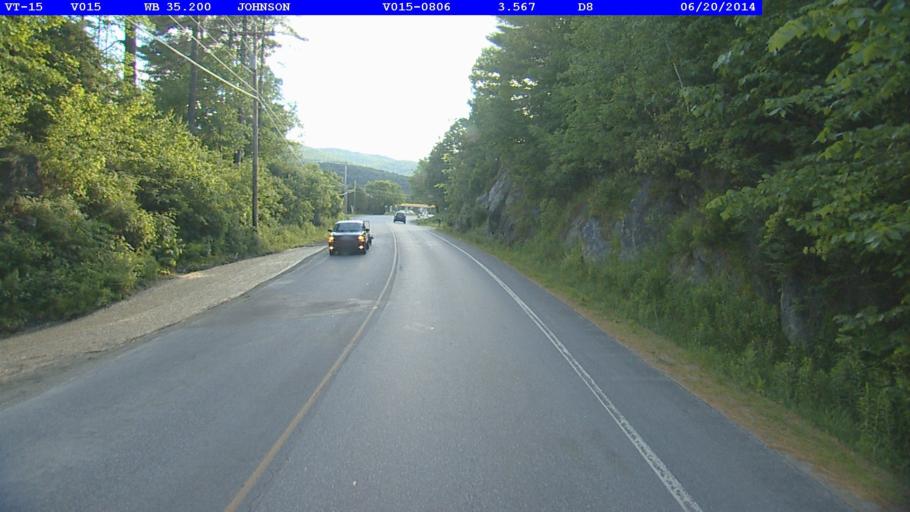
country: US
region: Vermont
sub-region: Lamoille County
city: Johnson
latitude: 44.6362
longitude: -72.6898
